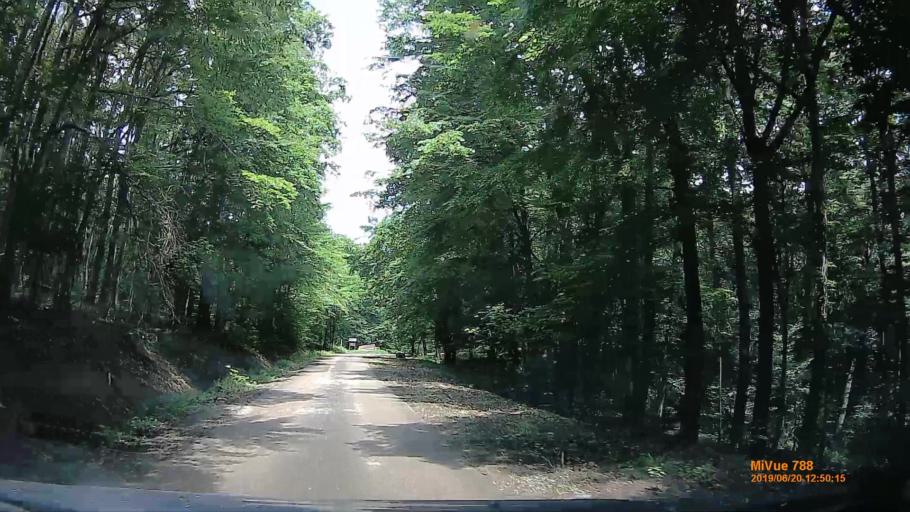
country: HU
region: Baranya
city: Hosszuheteny
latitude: 46.2135
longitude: 18.3507
